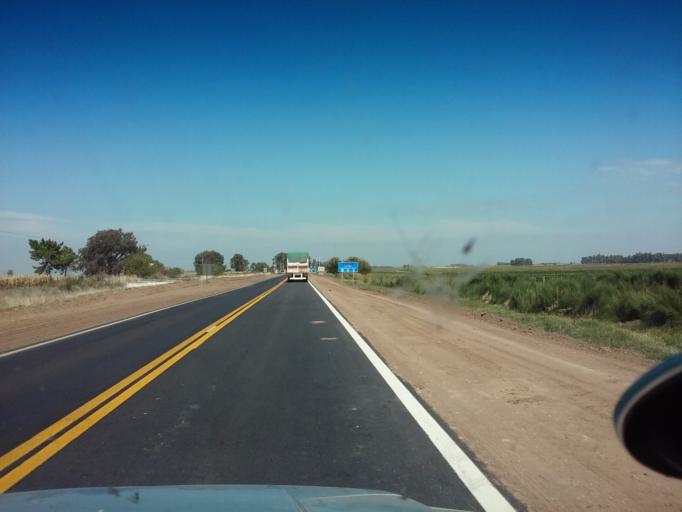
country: AR
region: Buenos Aires
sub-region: Partido de Nueve de Julio
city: Nueve de Julio
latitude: -35.3564
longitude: -60.6982
